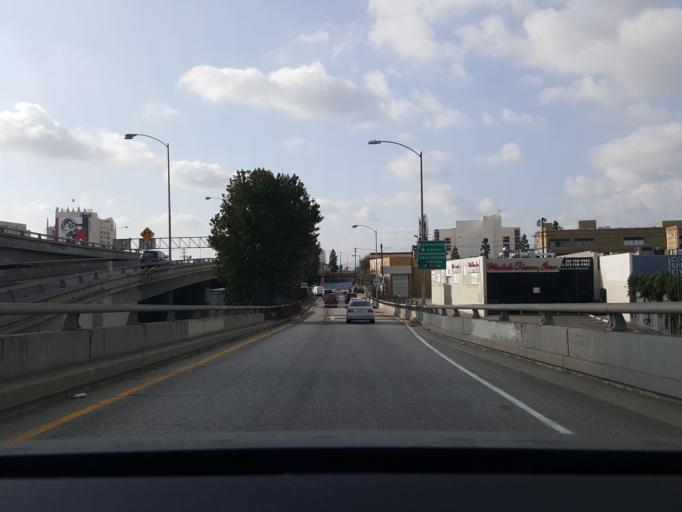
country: US
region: California
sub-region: Los Angeles County
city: Los Angeles
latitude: 34.0318
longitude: -118.2605
